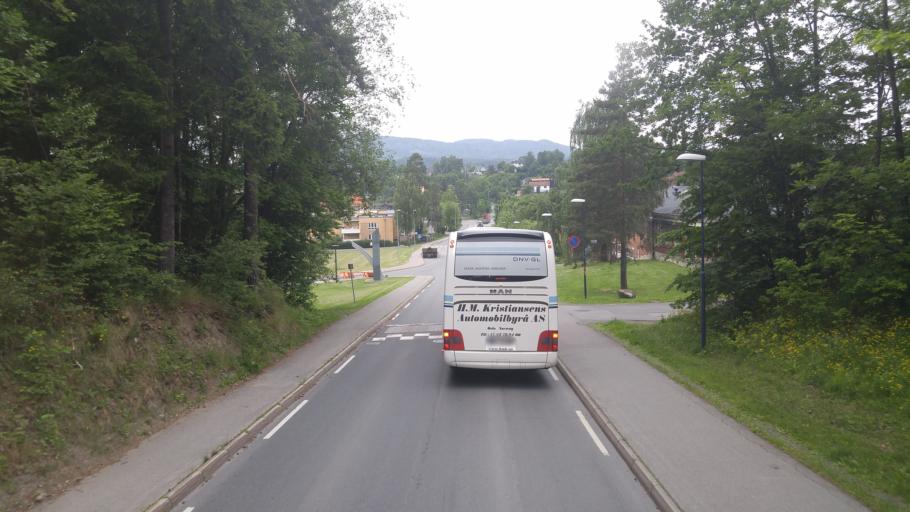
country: NO
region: Akershus
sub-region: Baerum
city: Sandvika
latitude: 59.8910
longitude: 10.5578
